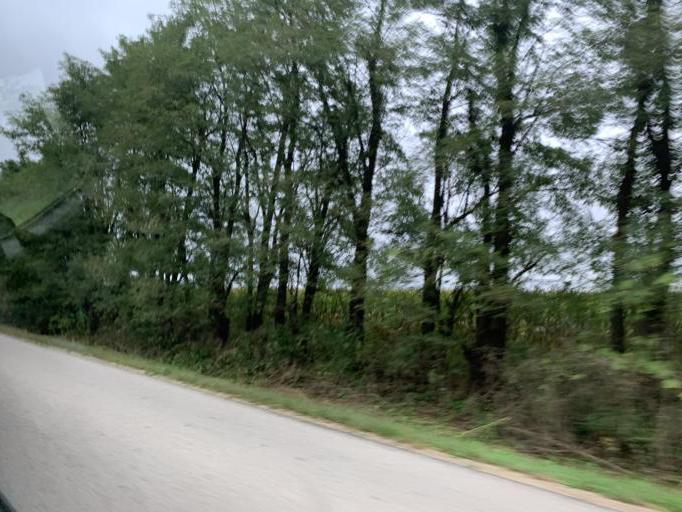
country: US
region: Wisconsin
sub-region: Sauk County
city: Prairie du Sac
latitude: 43.3014
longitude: -89.7789
